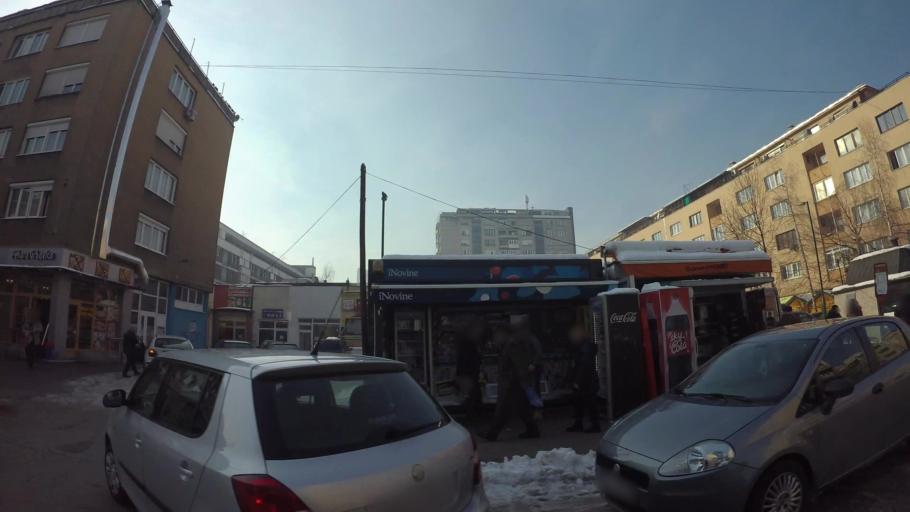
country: BA
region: Federation of Bosnia and Herzegovina
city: Kobilja Glava
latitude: 43.8507
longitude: 18.3956
